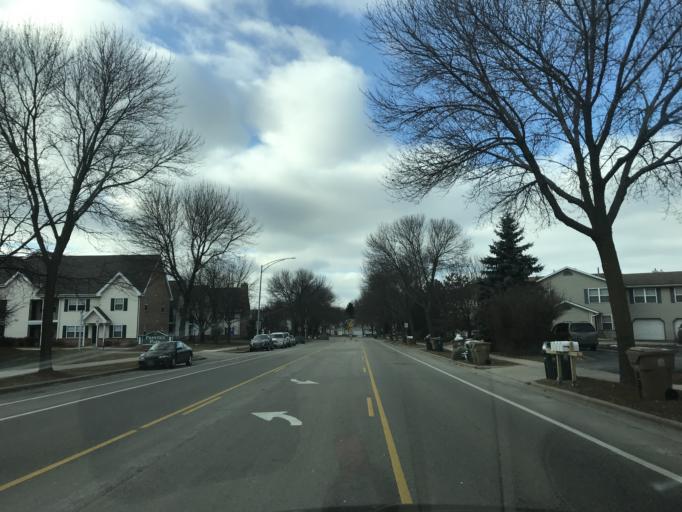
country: US
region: Wisconsin
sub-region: Dane County
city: Monona
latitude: 43.1092
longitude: -89.2977
